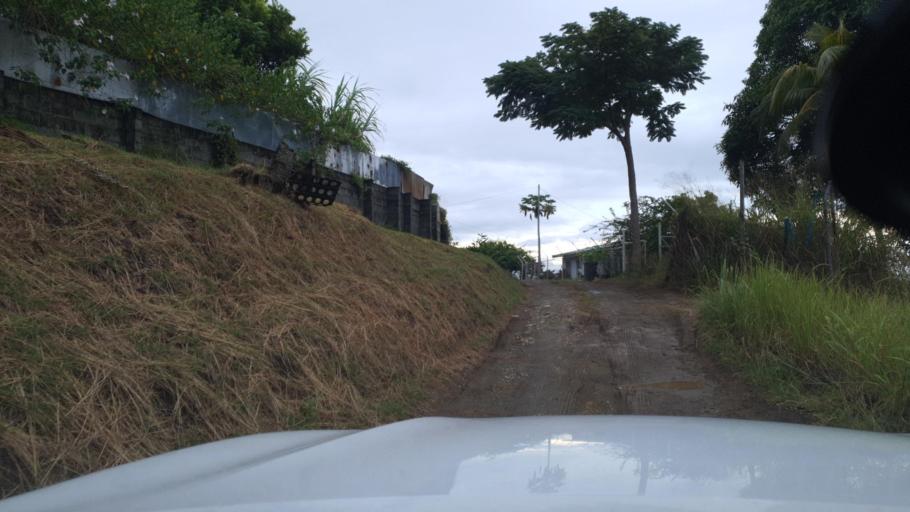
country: SB
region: Guadalcanal
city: Honiara
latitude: -9.4401
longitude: 159.9680
